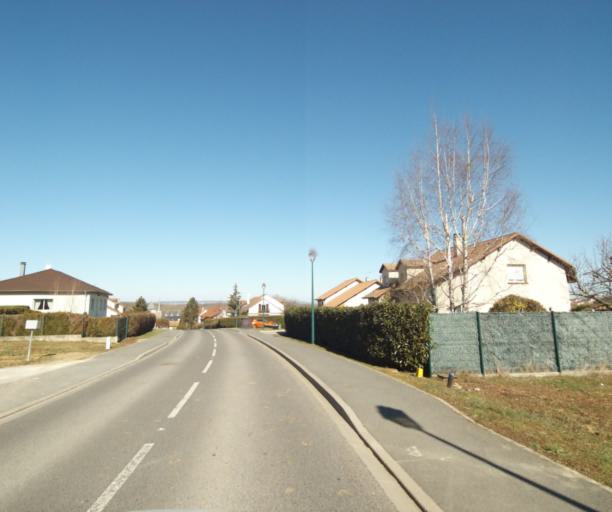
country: FR
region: Lorraine
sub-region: Departement de Meurthe-et-Moselle
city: Fleville-devant-Nancy
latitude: 48.6216
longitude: 6.2023
